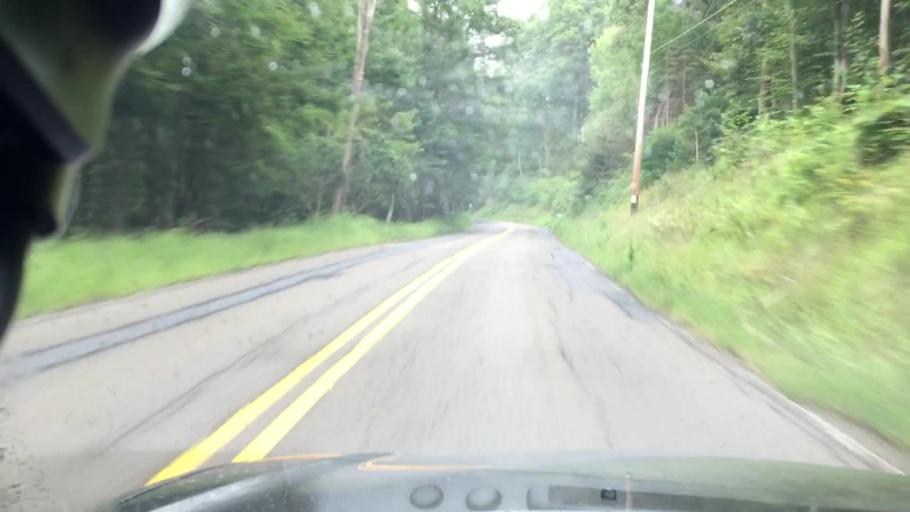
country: US
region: Pennsylvania
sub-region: Luzerne County
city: Harleigh
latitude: 41.0001
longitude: -75.9997
